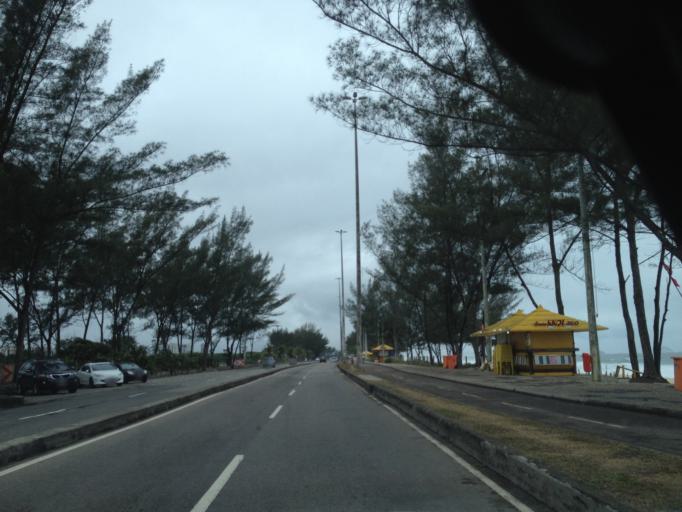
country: BR
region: Rio de Janeiro
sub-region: Nilopolis
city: Nilopolis
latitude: -23.0221
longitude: -43.4459
